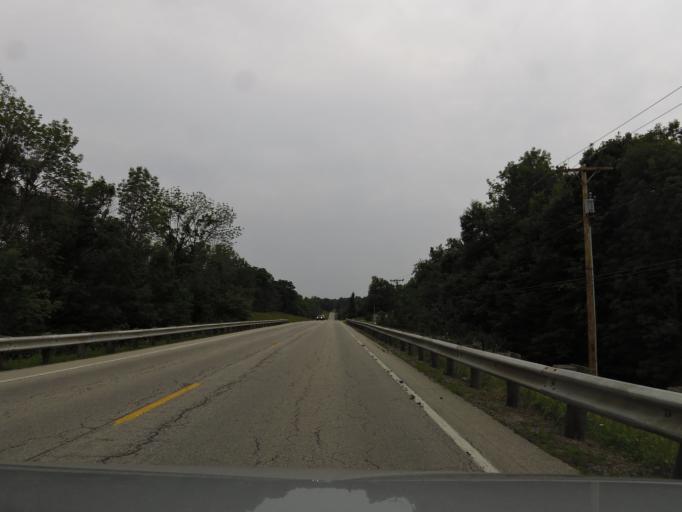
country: US
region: Ohio
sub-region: Clinton County
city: Wilmington
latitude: 39.3892
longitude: -83.8597
